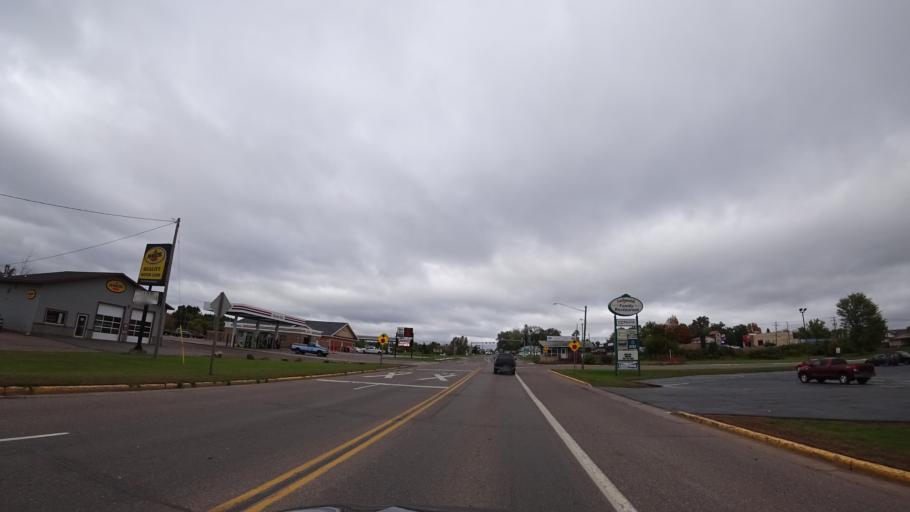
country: US
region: Wisconsin
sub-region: Rusk County
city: Ladysmith
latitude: 45.4636
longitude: -91.1111
